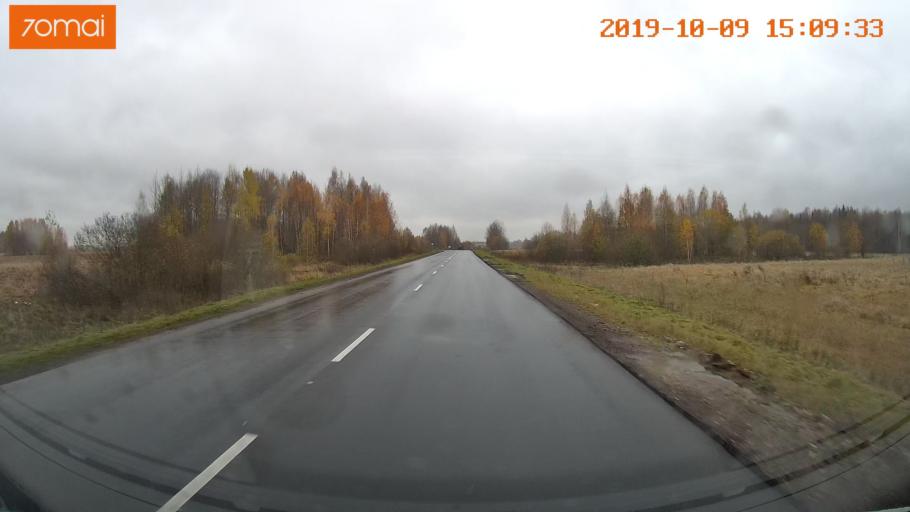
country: RU
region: Kostroma
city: Susanino
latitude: 58.1900
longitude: 41.6498
